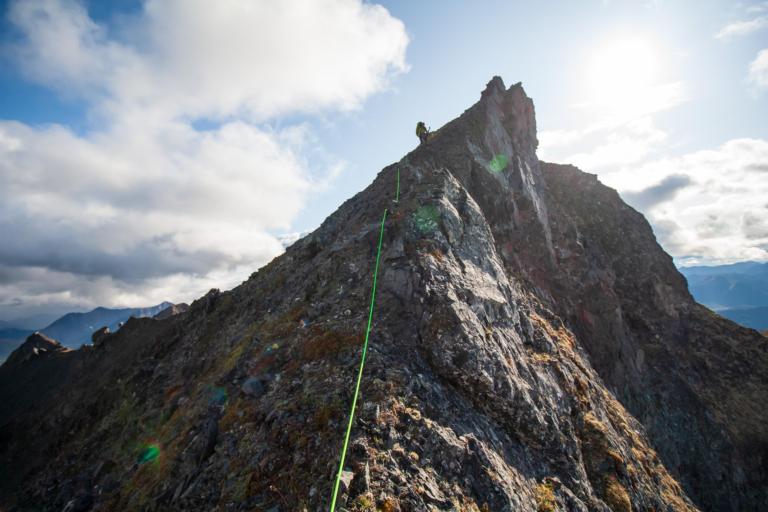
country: RU
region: Kamtsjatka
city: Yelizovo
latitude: 53.8514
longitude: 158.1892
